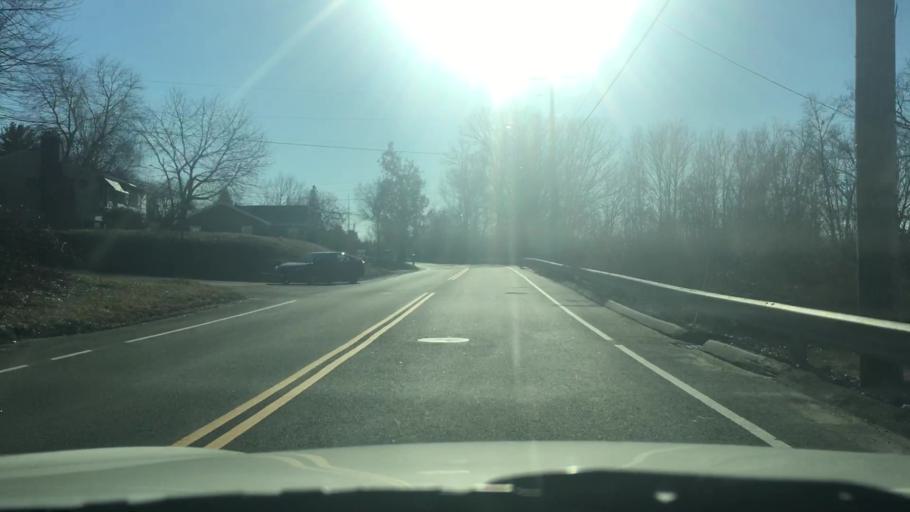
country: US
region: Massachusetts
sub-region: Hampden County
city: Ludlow
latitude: 42.1866
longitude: -72.5047
